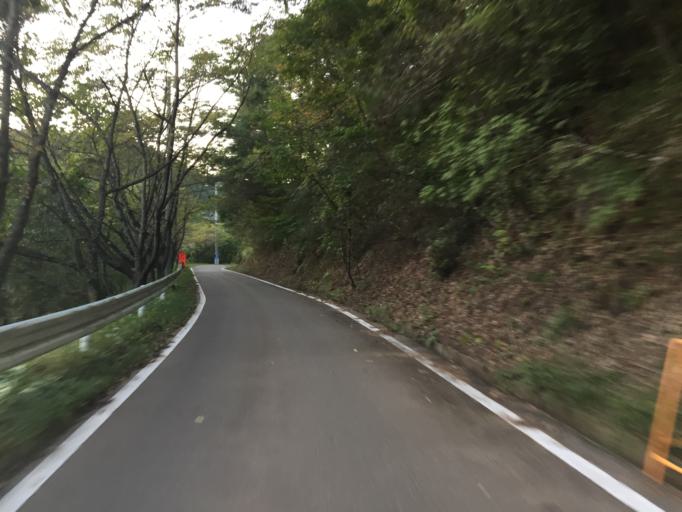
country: JP
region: Fukushima
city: Yanagawamachi-saiwaicho
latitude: 37.8488
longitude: 140.6323
